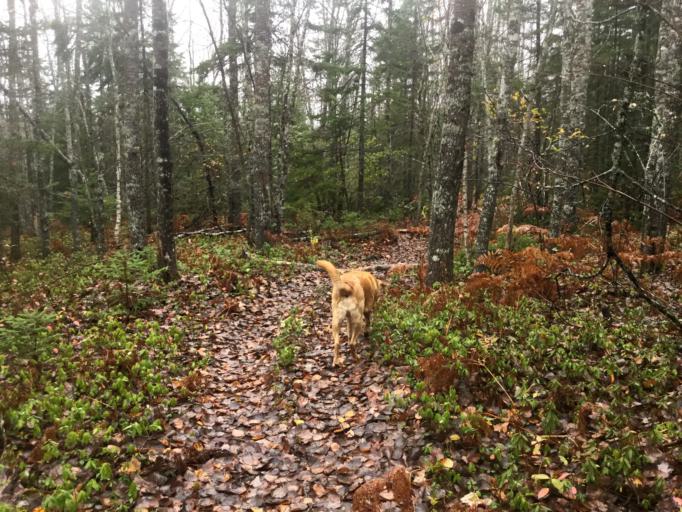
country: CA
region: Nova Scotia
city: New Glasgow
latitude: 45.5495
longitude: -62.6813
